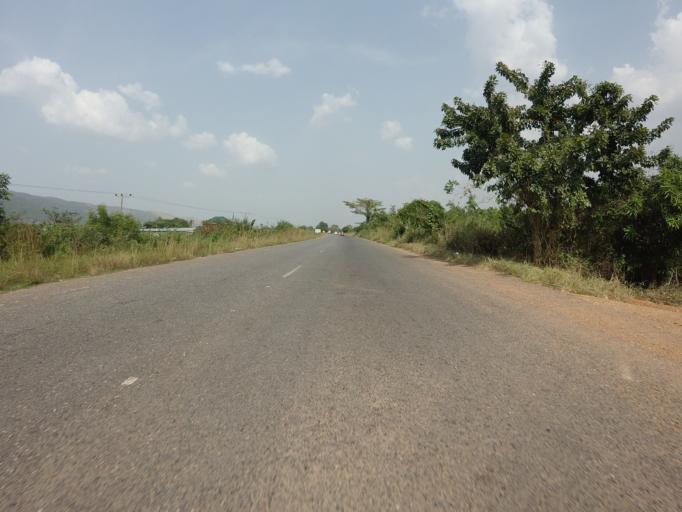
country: GH
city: Akropong
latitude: 5.9354
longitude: -0.0319
